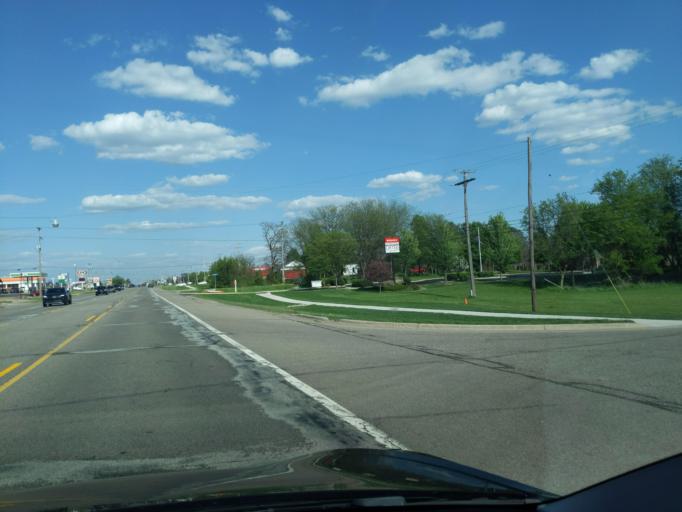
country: US
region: Michigan
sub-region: Eaton County
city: Grand Ledge
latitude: 42.7408
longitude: -84.7465
